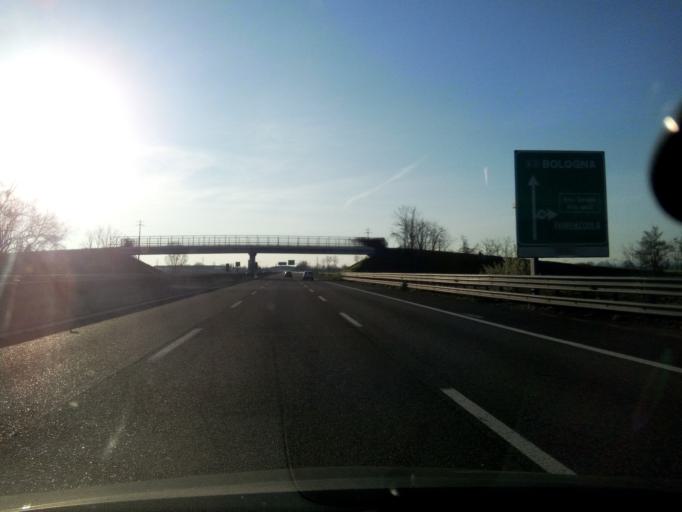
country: IT
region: Emilia-Romagna
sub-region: Provincia di Piacenza
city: Roveleto
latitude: 44.9693
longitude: 9.8896
